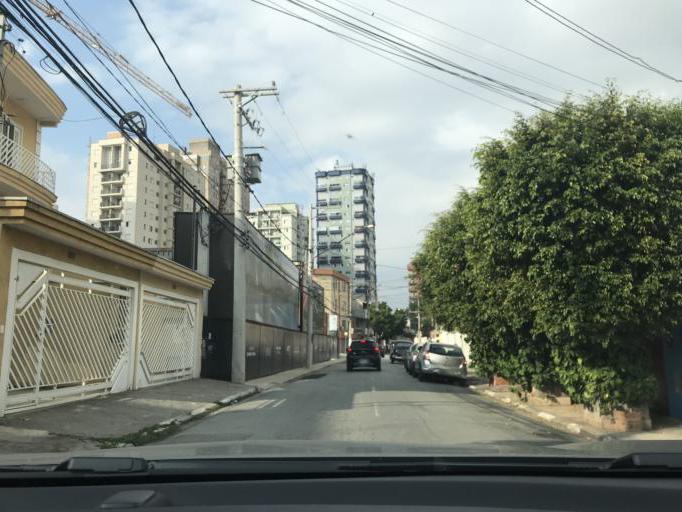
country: BR
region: Sao Paulo
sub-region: Osasco
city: Osasco
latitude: -23.5404
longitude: -46.7770
